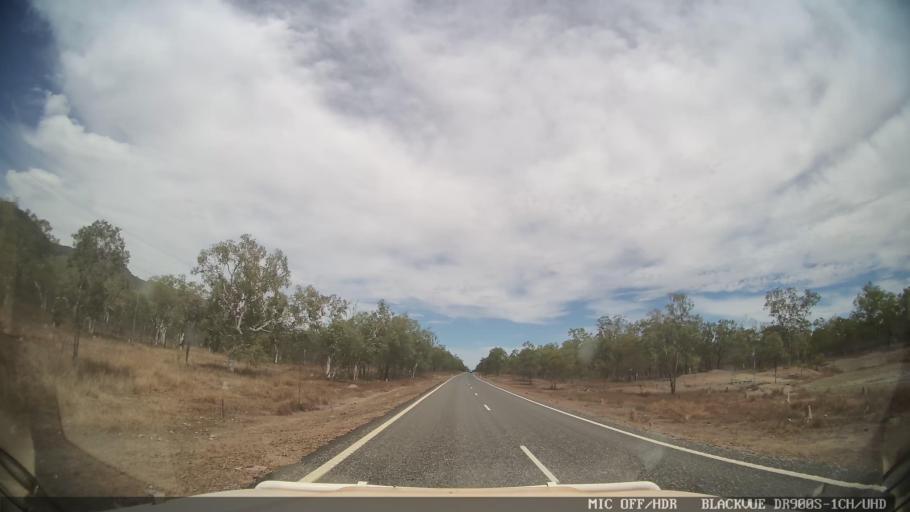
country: AU
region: Queensland
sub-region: Cairns
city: Port Douglas
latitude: -16.2431
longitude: 144.7270
